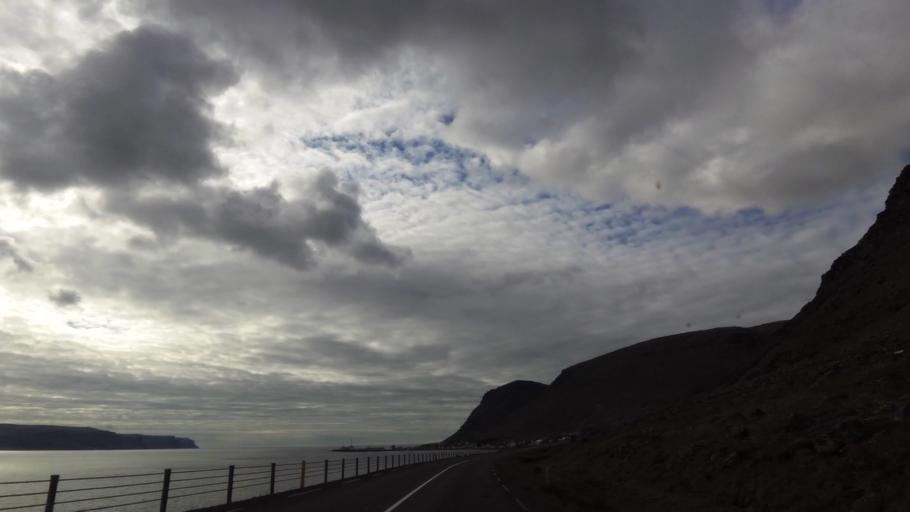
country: IS
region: West
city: Olafsvik
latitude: 65.5836
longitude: -23.9647
